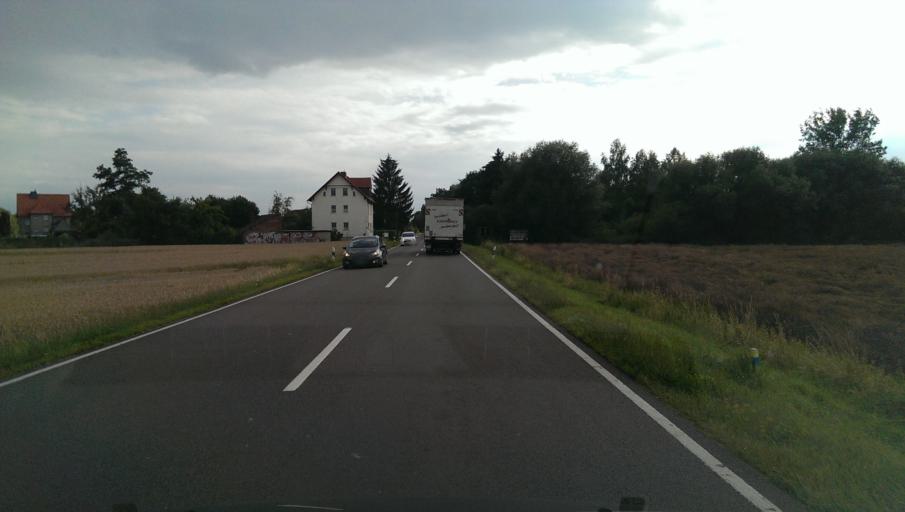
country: DE
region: Saxony
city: Elstertrebnitz
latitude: 51.1329
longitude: 12.2211
